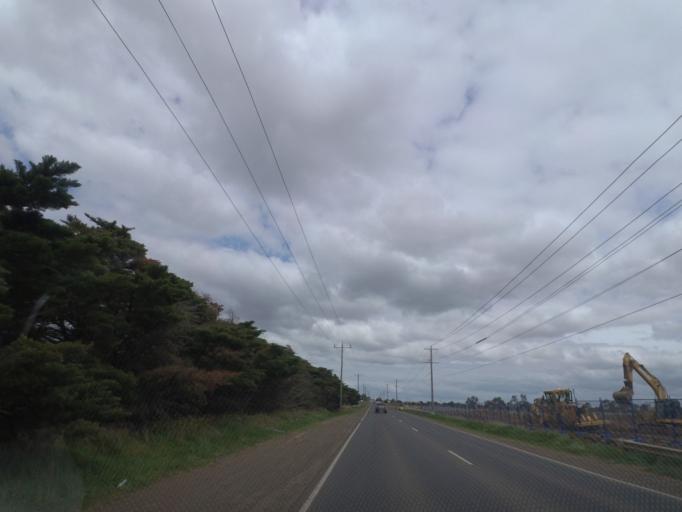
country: AU
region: Victoria
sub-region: Wyndham
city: Williams Landing
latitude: -37.8472
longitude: 144.7460
